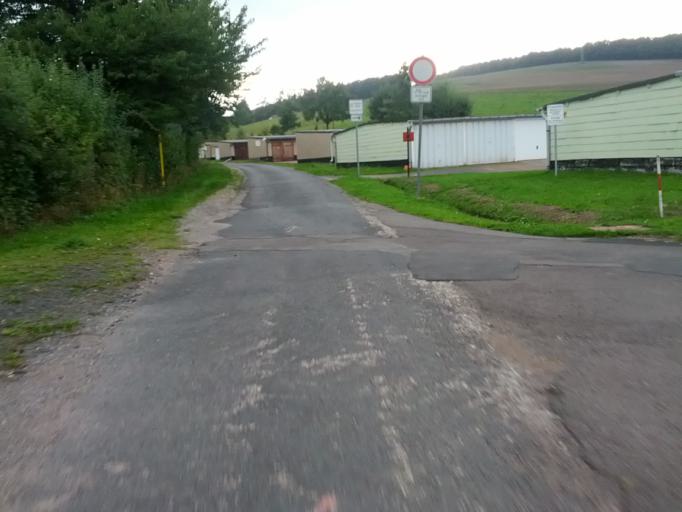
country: DE
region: Thuringia
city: Thal
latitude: 50.9514
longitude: 10.3886
